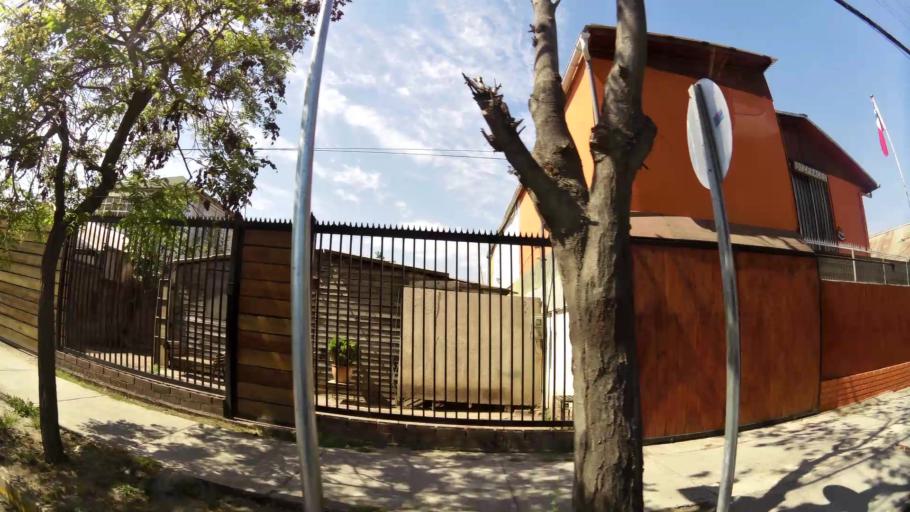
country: CL
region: Santiago Metropolitan
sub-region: Provincia de Santiago
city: La Pintana
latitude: -33.5548
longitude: -70.6662
